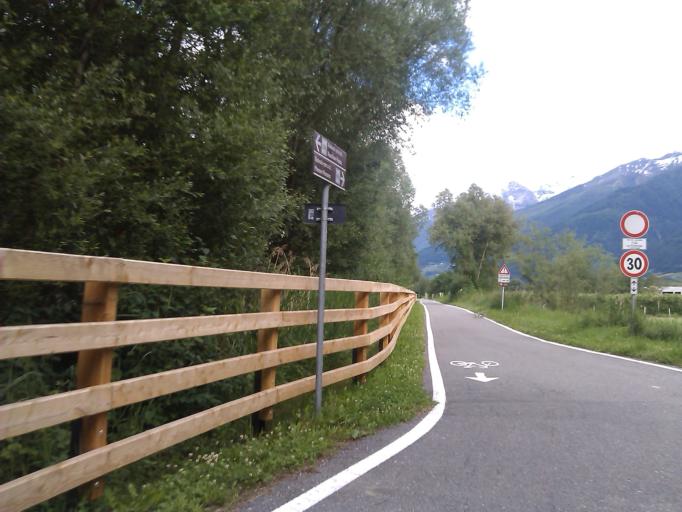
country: IT
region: Trentino-Alto Adige
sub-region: Bolzano
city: Prato Allo Stelvio
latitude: 46.6414
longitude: 10.5907
